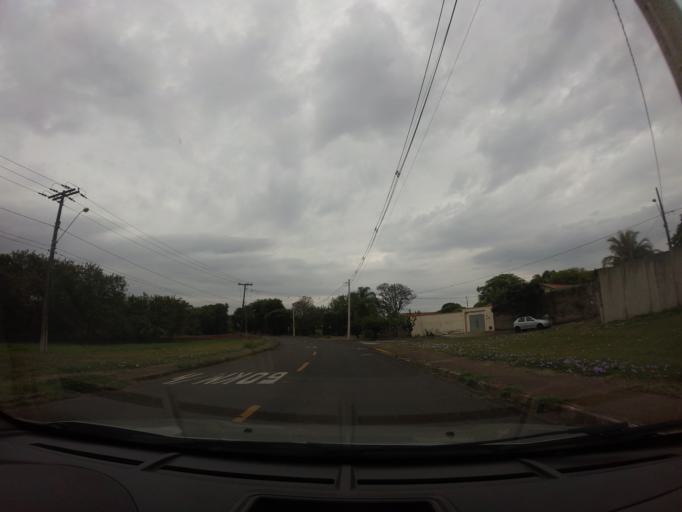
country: BR
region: Sao Paulo
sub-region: Piracicaba
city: Piracicaba
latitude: -22.7503
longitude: -47.5927
